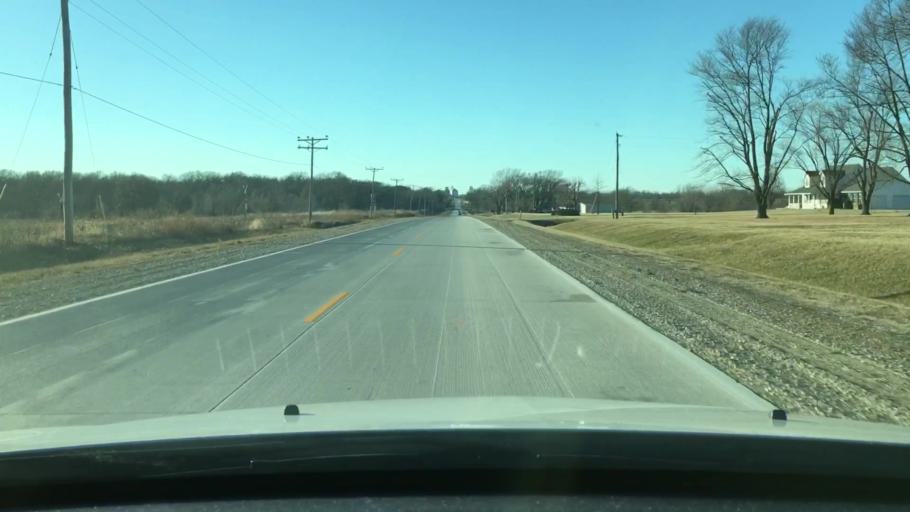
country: US
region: Missouri
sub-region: Boone County
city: Centralia
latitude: 39.2064
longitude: -92.0950
